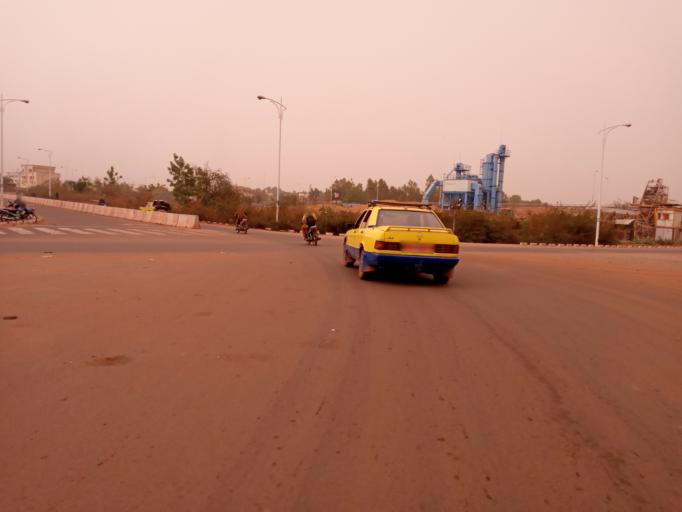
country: ML
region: Bamako
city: Bamako
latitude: 12.6485
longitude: -7.9306
